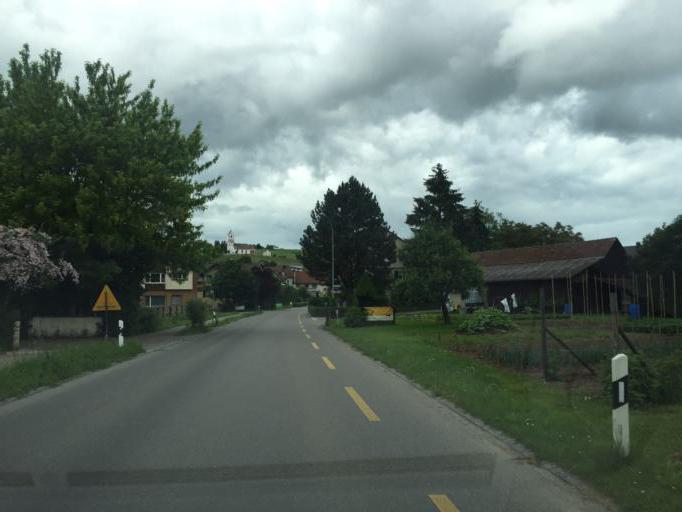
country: CH
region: Schaffhausen
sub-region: Bezirk Unterklettgau
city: Hallau
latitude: 47.6956
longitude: 8.4651
